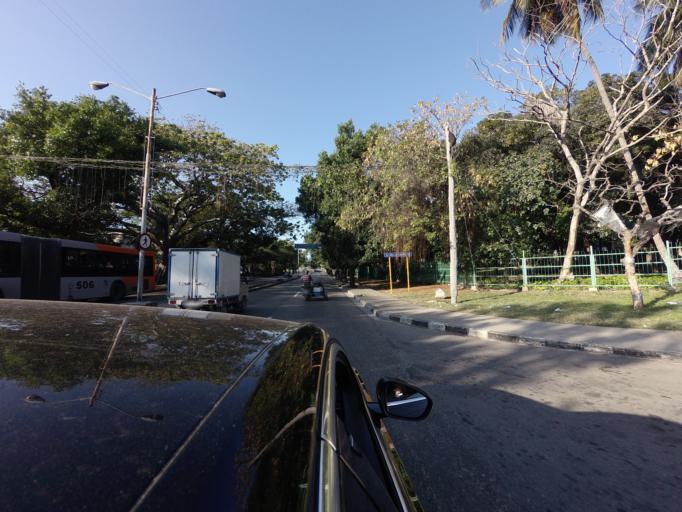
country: CU
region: La Habana
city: Cerro
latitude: 23.0862
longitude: -82.4280
